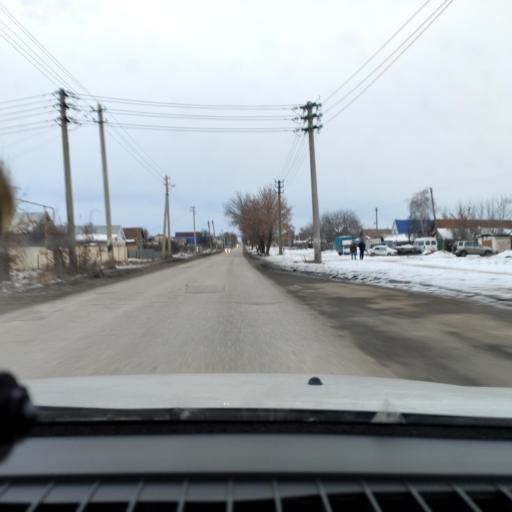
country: RU
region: Samara
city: Chapayevsk
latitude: 52.9958
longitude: 49.7153
